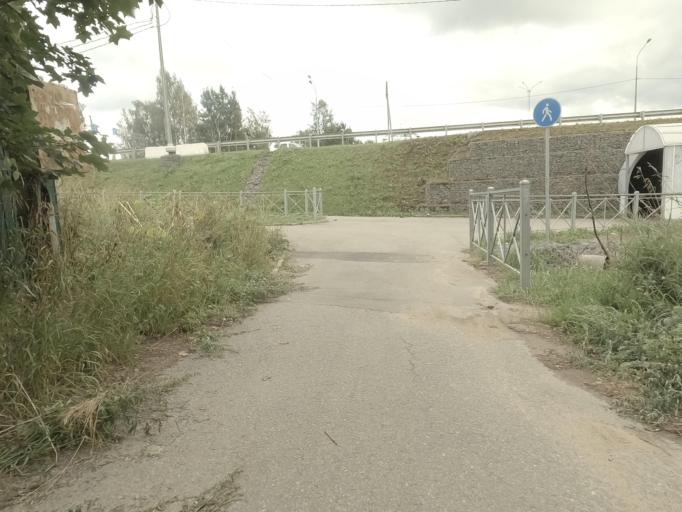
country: RU
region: Leningrad
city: Koltushi
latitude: 59.8980
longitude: 30.6849
